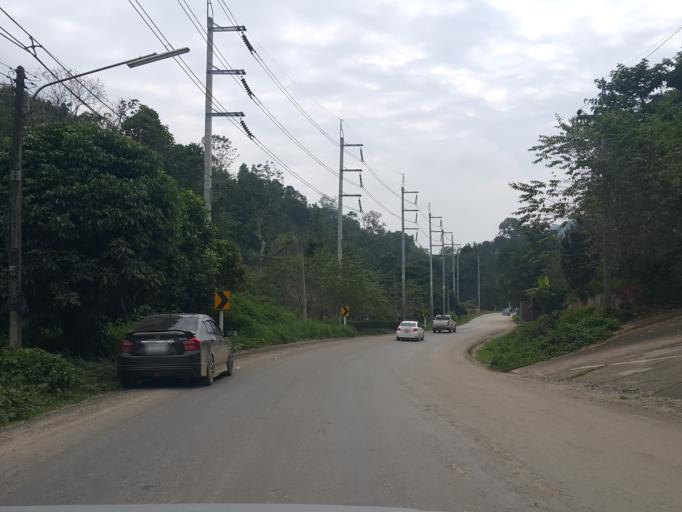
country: TH
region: Chiang Mai
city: Mae Taeng
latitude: 19.1685
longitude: 98.6914
